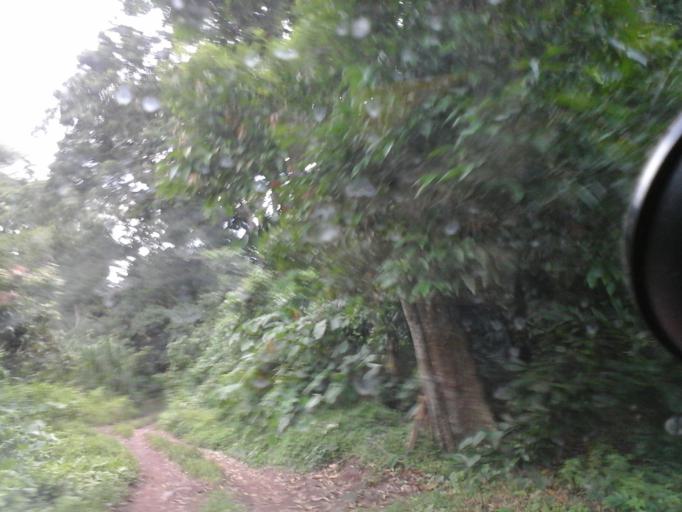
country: CO
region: Cesar
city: San Diego
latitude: 10.2806
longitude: -73.0902
